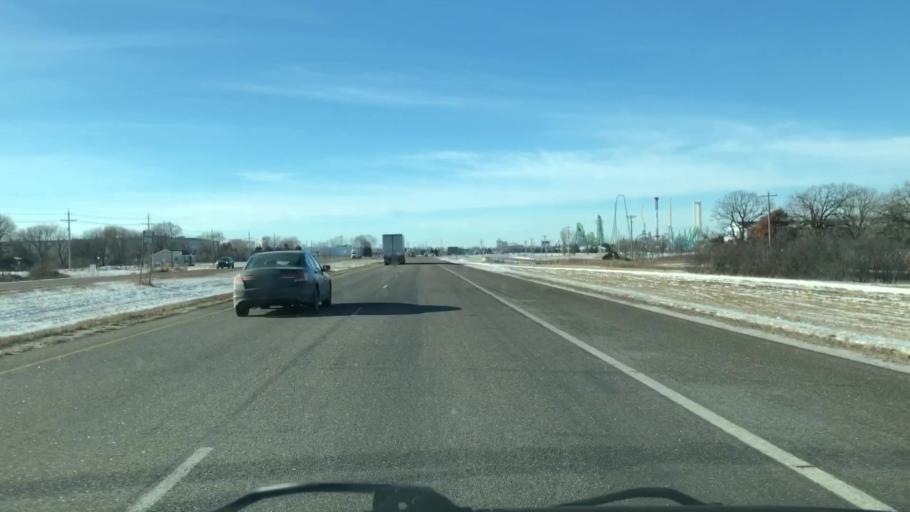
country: US
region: Minnesota
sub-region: Hennepin County
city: Eden Prairie
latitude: 44.7960
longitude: -93.4404
